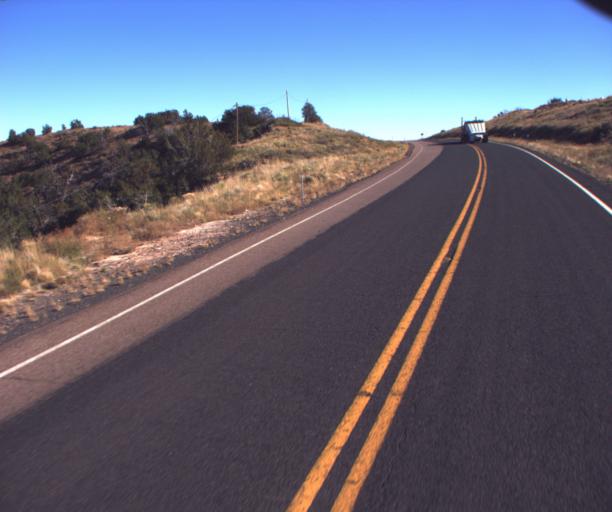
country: US
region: Arizona
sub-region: Apache County
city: Ganado
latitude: 35.4348
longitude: -109.5225
